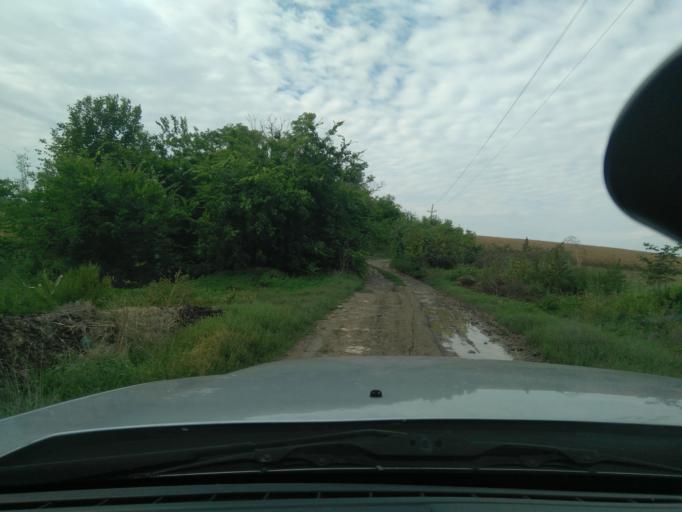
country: HU
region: Fejer
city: Val
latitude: 47.3731
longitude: 18.7264
